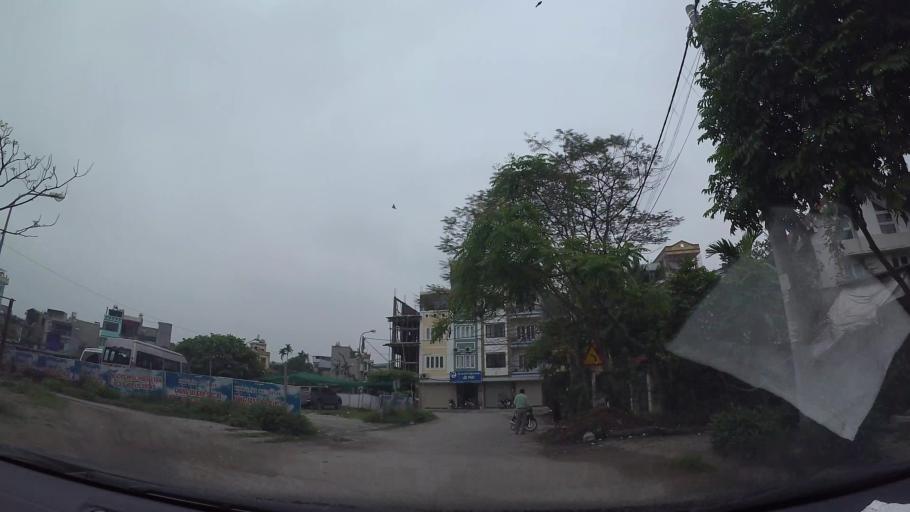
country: VN
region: Ha Noi
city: Hai BaTrung
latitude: 20.9979
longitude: 105.8832
